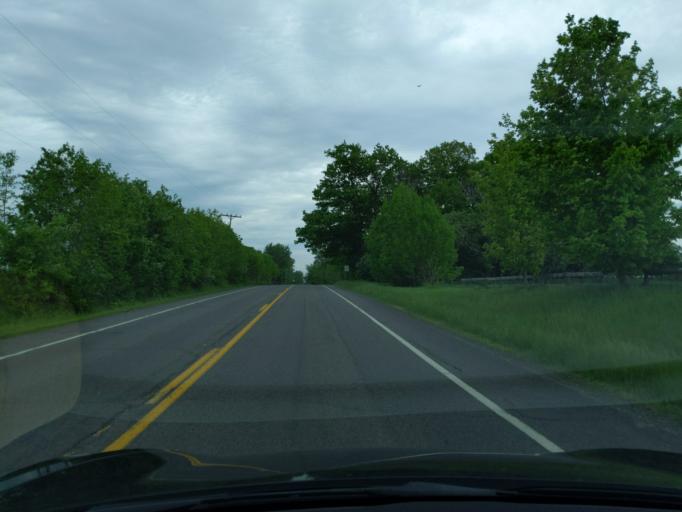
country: US
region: Michigan
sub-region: Ingham County
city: Mason
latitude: 42.5770
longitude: -84.3571
